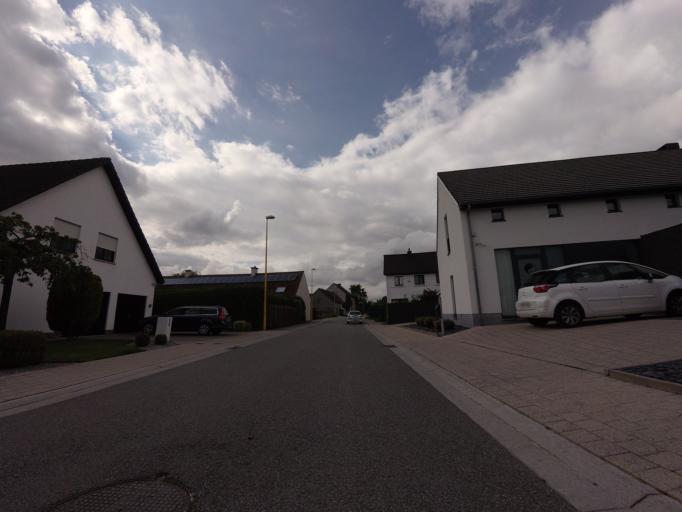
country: BE
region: Flanders
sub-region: Provincie Vlaams-Brabant
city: Grimbergen
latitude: 50.9357
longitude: 4.3591
